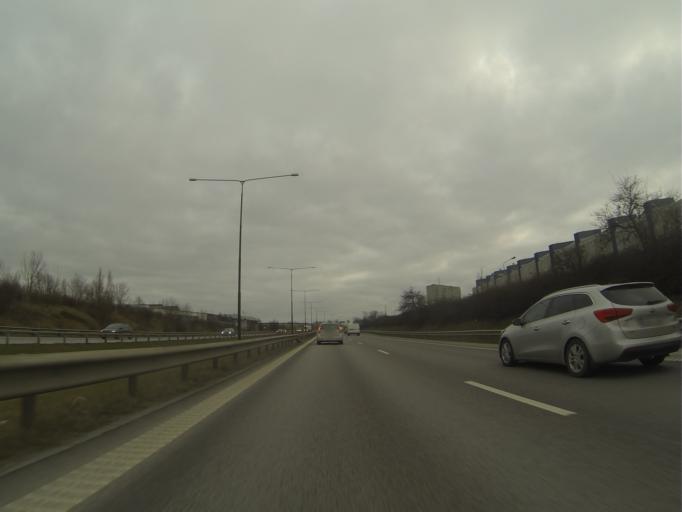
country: SE
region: Skane
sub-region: Burlovs Kommun
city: Arloev
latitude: 55.5886
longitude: 13.0555
